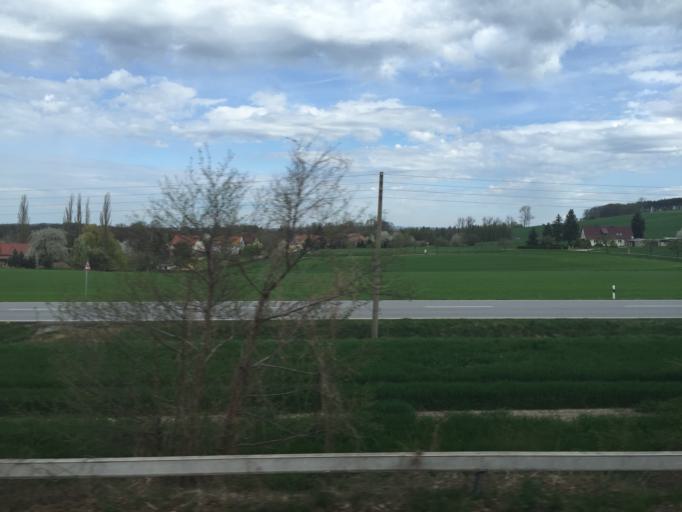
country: DE
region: Saxony
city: Sohland am Rotstein
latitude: 51.1187
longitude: 14.7264
